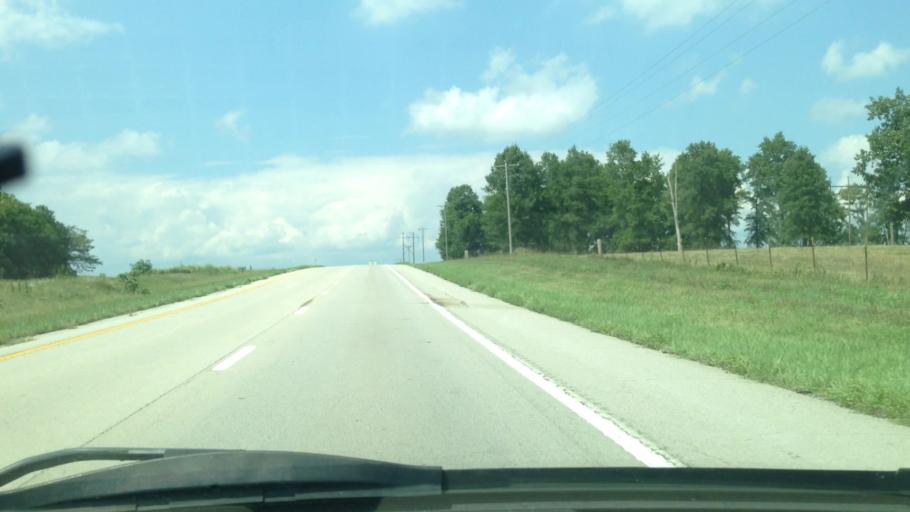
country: US
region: Missouri
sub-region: Lincoln County
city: Troy
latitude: 39.1464
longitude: -90.9683
